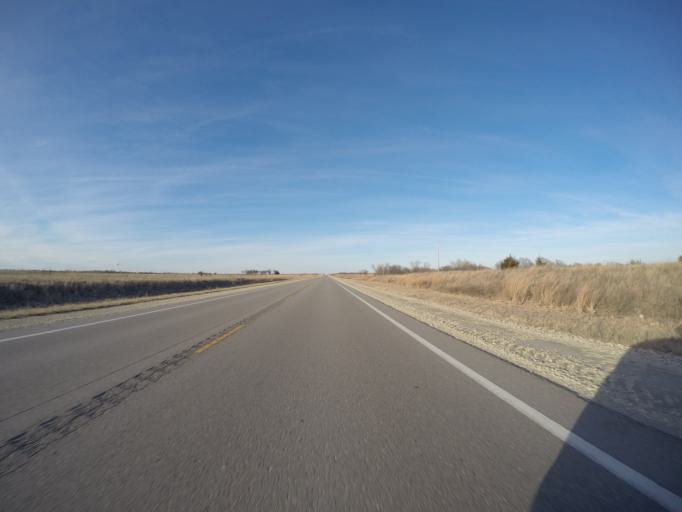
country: US
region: Kansas
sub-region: Marion County
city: Marion
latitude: 38.3113
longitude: -96.9666
